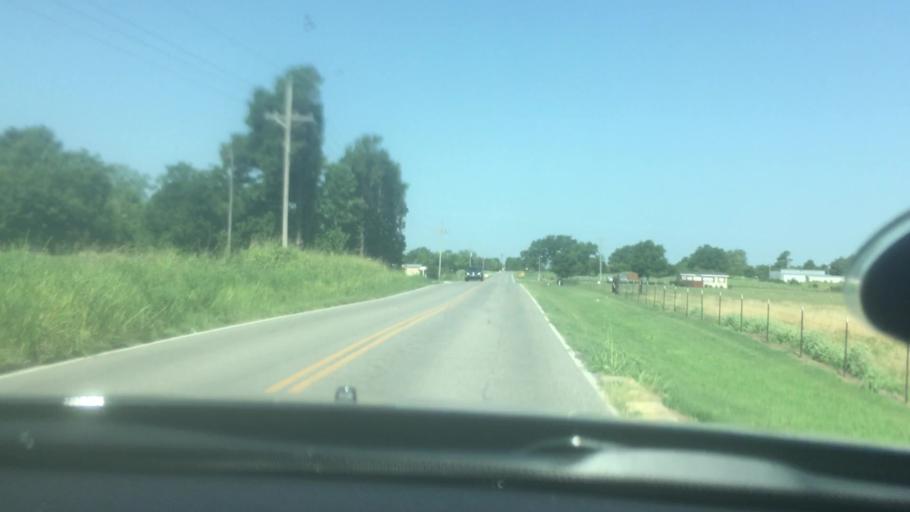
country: US
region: Oklahoma
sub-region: Bryan County
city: Calera
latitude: 34.0198
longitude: -96.4691
